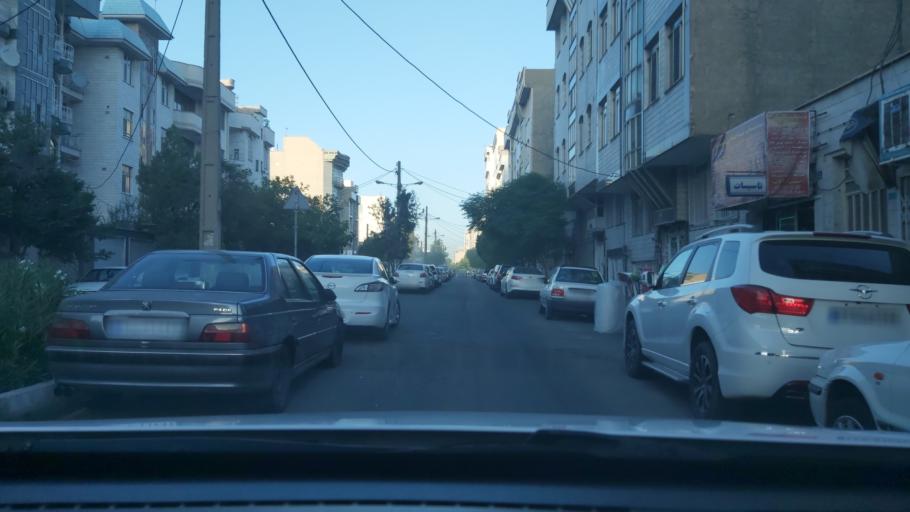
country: IR
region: Tehran
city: Tehran
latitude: 35.7315
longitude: 51.3055
